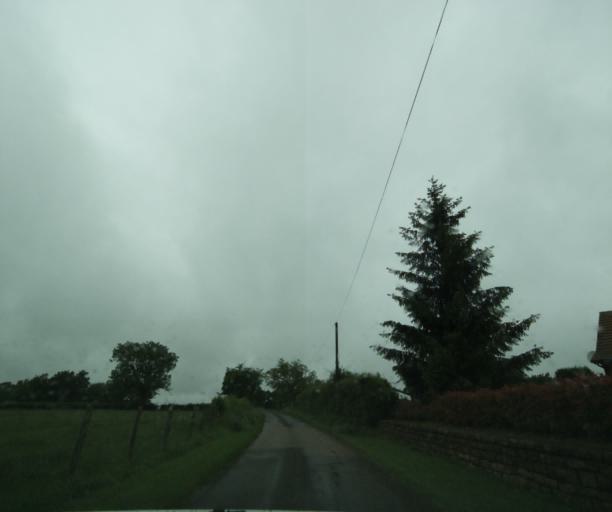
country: FR
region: Bourgogne
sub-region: Departement de Saone-et-Loire
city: Charolles
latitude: 46.4066
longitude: 4.3246
